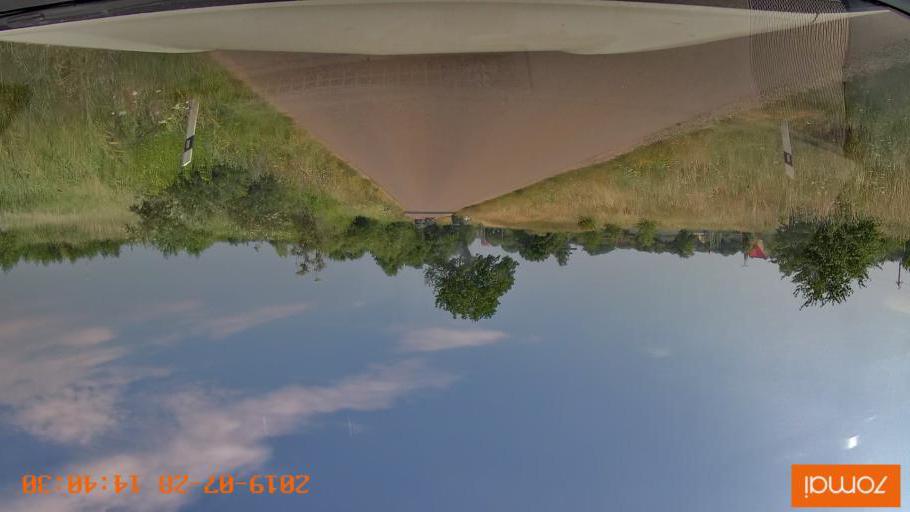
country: RU
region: Kaliningrad
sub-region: Gorod Kaliningrad
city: Yantarnyy
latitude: 54.8518
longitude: 19.9572
